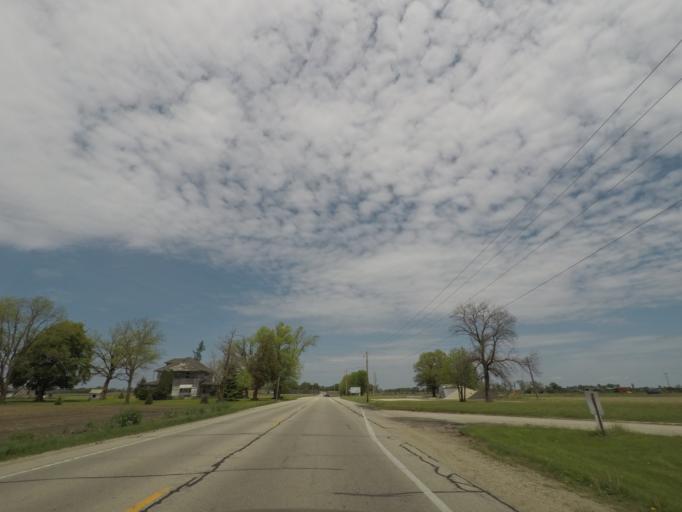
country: US
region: Wisconsin
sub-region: Rock County
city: Evansville
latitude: 42.8080
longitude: -89.2991
